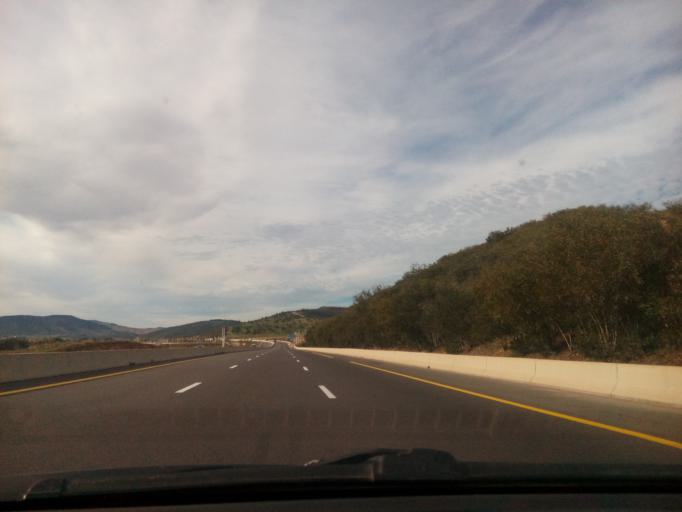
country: DZ
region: Sidi Bel Abbes
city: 'Ain el Berd
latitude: 35.4357
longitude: -0.4491
